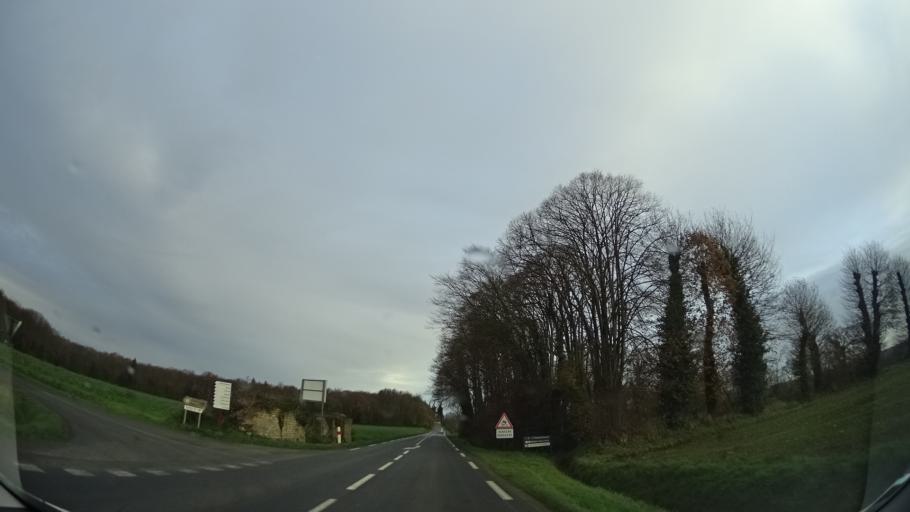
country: FR
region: Brittany
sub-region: Departement des Cotes-d'Armor
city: Evran
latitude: 48.3914
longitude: -1.9798
